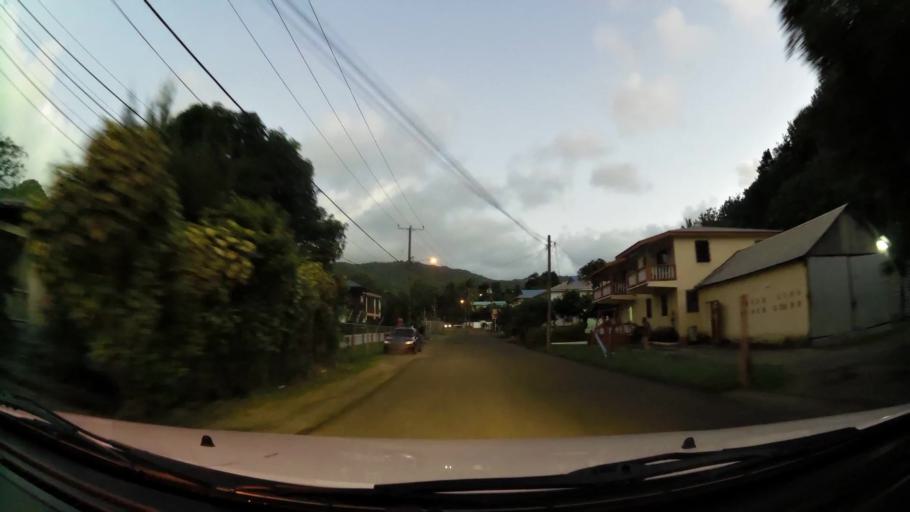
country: LC
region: Castries Quarter
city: Bisee
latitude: 14.0391
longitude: -60.9543
